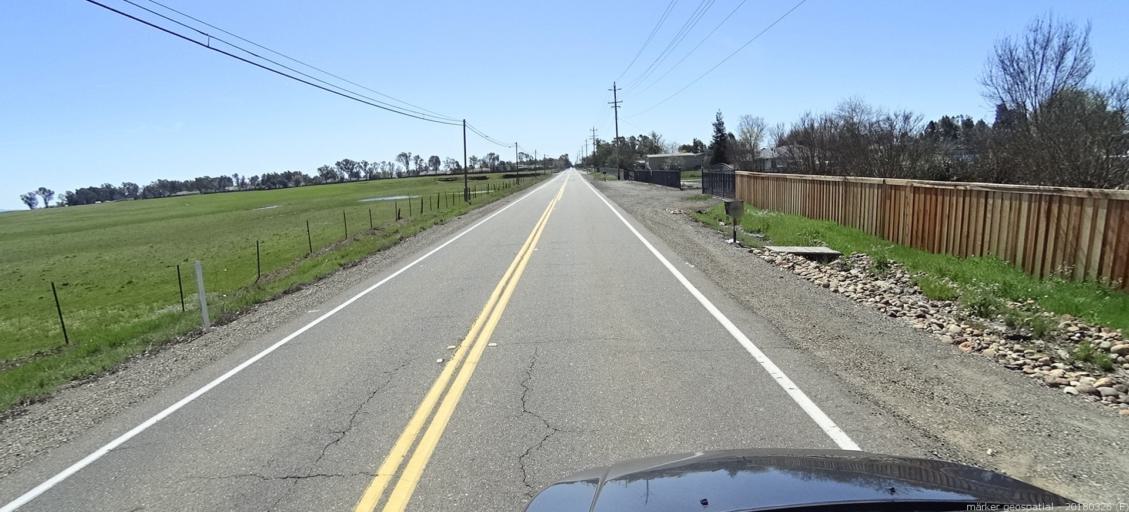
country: US
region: California
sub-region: Sacramento County
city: Vineyard
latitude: 38.4727
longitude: -121.2977
